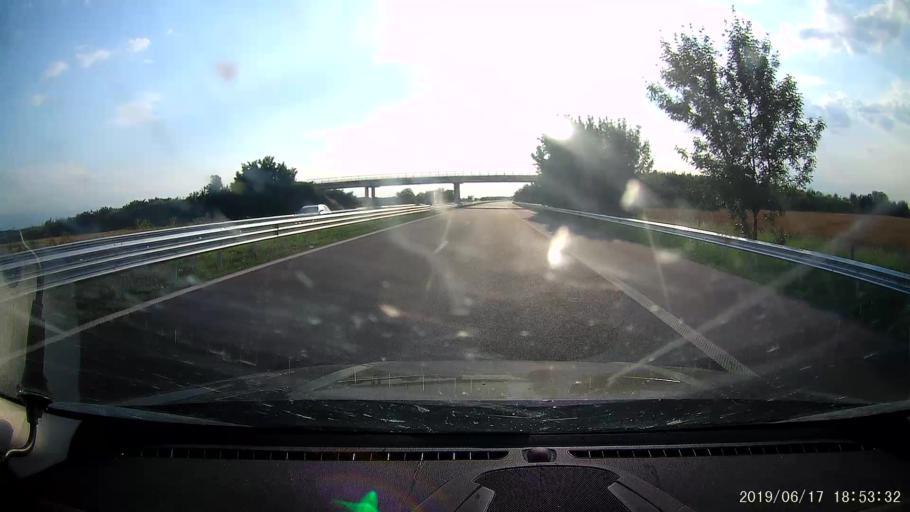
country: BG
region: Plovdiv
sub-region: Obshtina Sadovo
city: Sadovo
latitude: 42.2163
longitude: 24.9086
